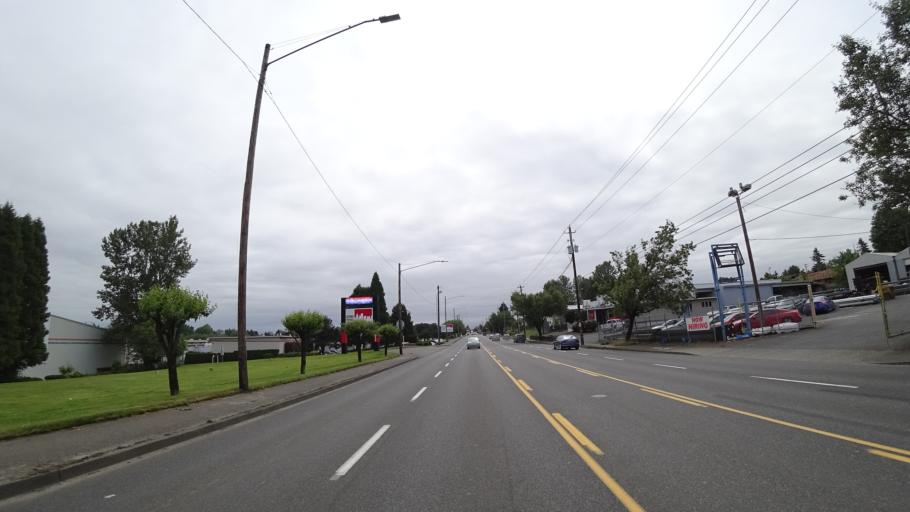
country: US
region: Oregon
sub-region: Multnomah County
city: Portland
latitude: 45.5697
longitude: -122.6066
